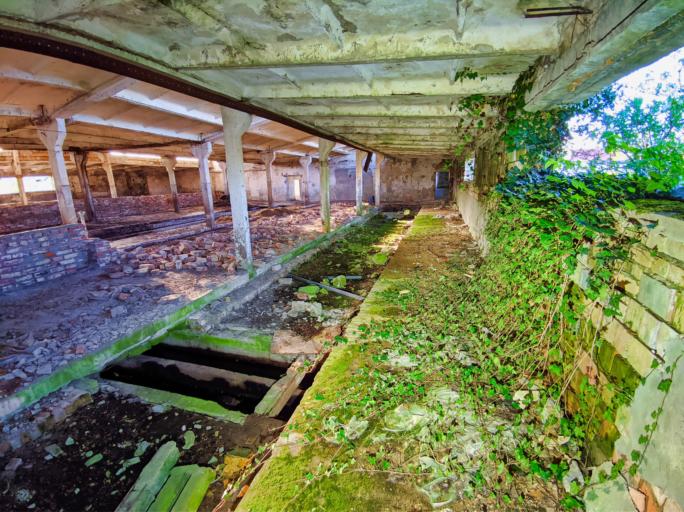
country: PL
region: Lubusz
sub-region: Powiat zaganski
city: Ilowa
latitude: 51.5431
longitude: 15.1958
